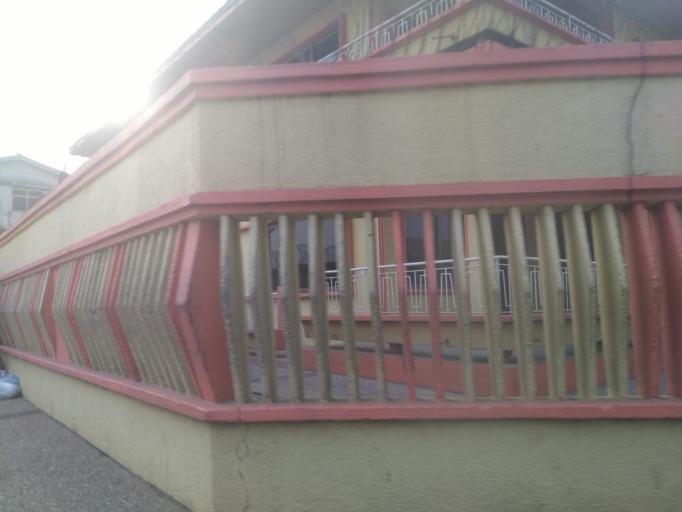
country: GH
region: Ashanti
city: Kumasi
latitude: 6.7049
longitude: -1.6174
